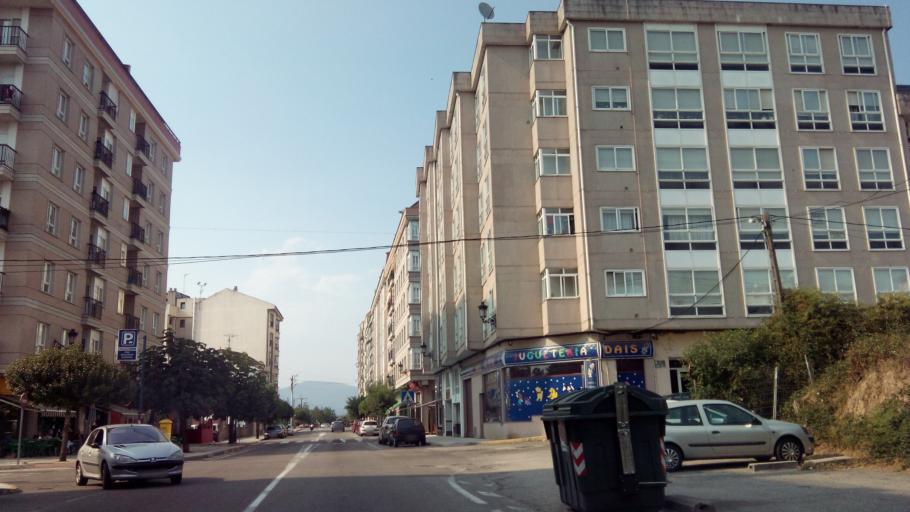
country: ES
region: Galicia
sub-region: Provincia de Pontevedra
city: Ponteareas
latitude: 42.1721
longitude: -8.5083
